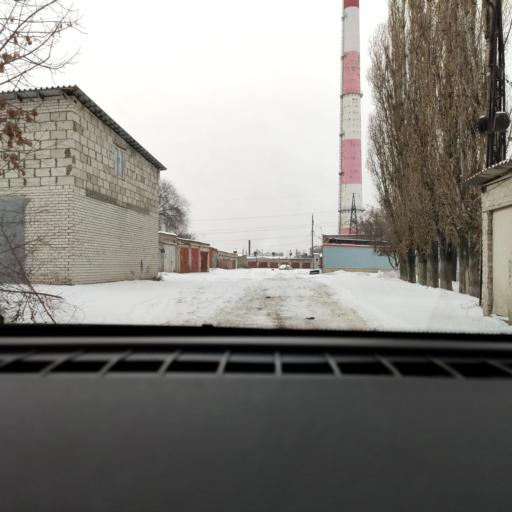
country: RU
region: Voronezj
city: Voronezh
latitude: 51.6336
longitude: 39.2509
